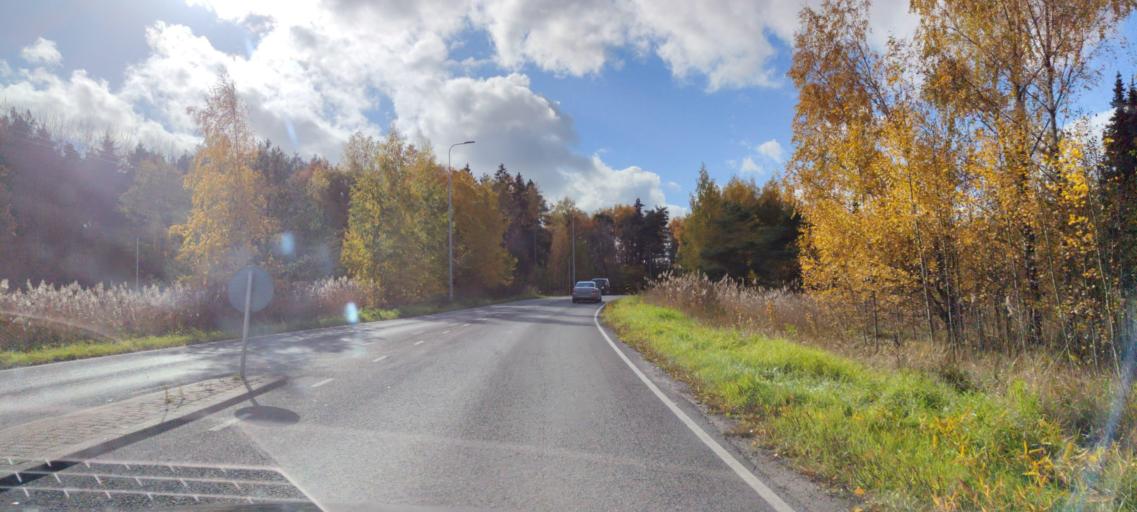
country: FI
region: Varsinais-Suomi
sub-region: Turku
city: Turku
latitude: 60.4206
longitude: 22.3000
